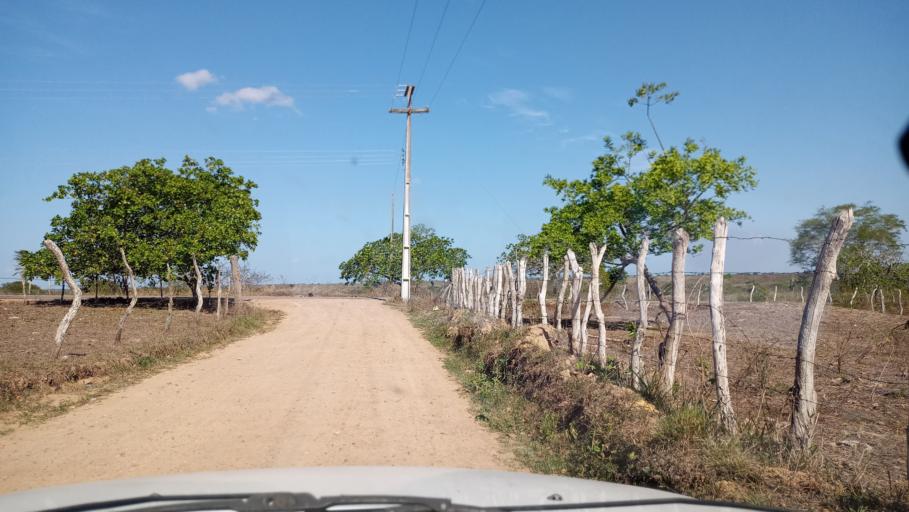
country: BR
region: Rio Grande do Norte
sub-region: Brejinho
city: Brejinho
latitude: -6.1795
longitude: -35.4498
